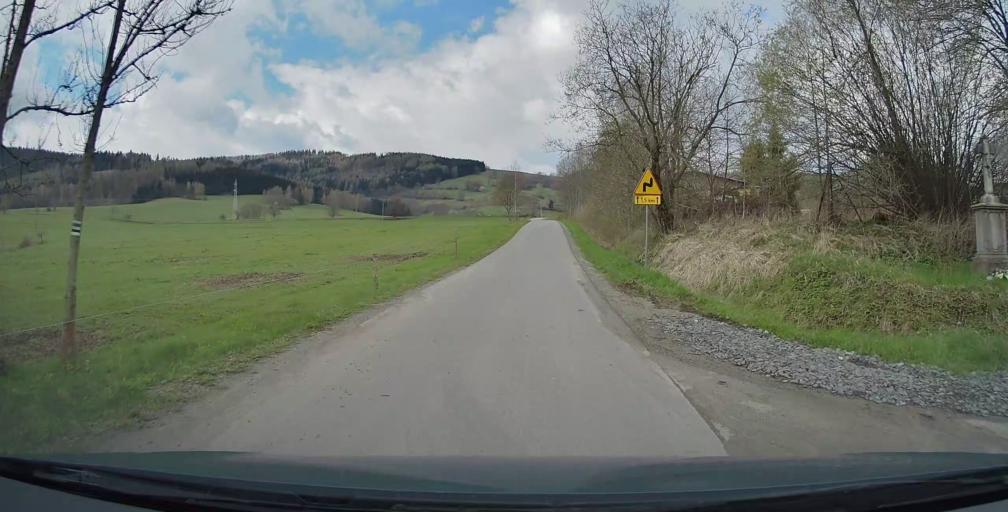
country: PL
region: Lower Silesian Voivodeship
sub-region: Powiat klodzki
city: Lewin Klodzki
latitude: 50.4046
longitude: 16.2763
